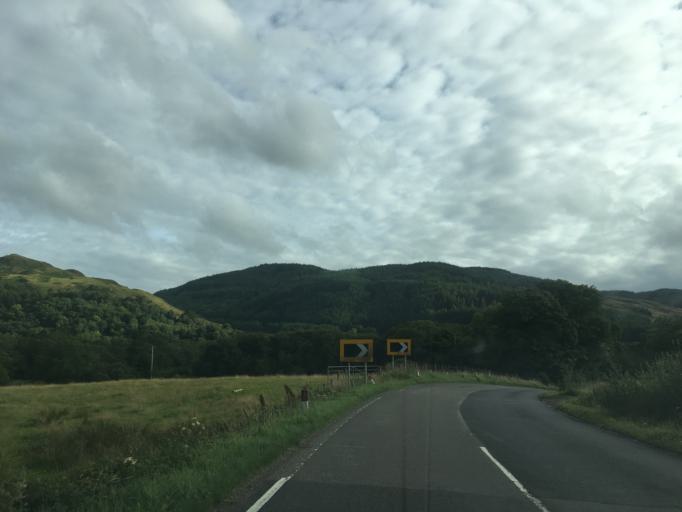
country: GB
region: Scotland
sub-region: Argyll and Bute
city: Oban
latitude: 56.3680
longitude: -5.4382
